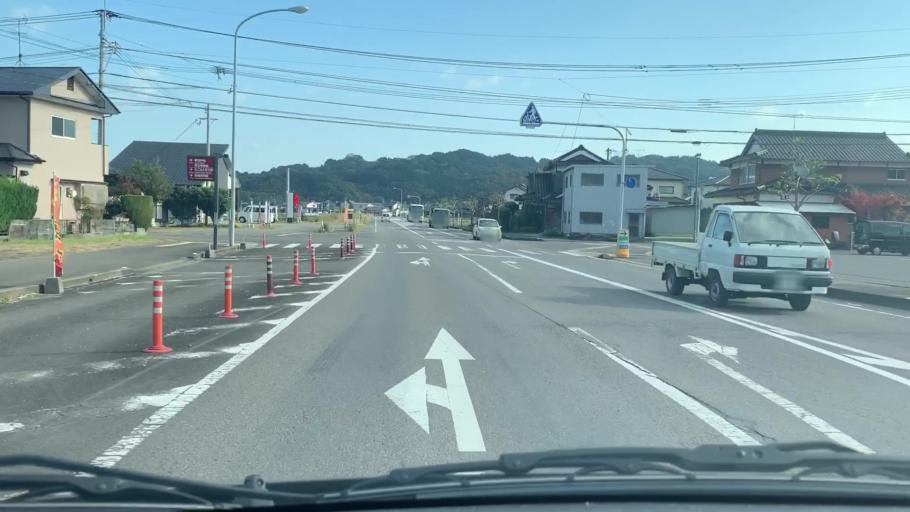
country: JP
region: Saga Prefecture
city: Kashima
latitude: 33.0937
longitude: 130.0943
